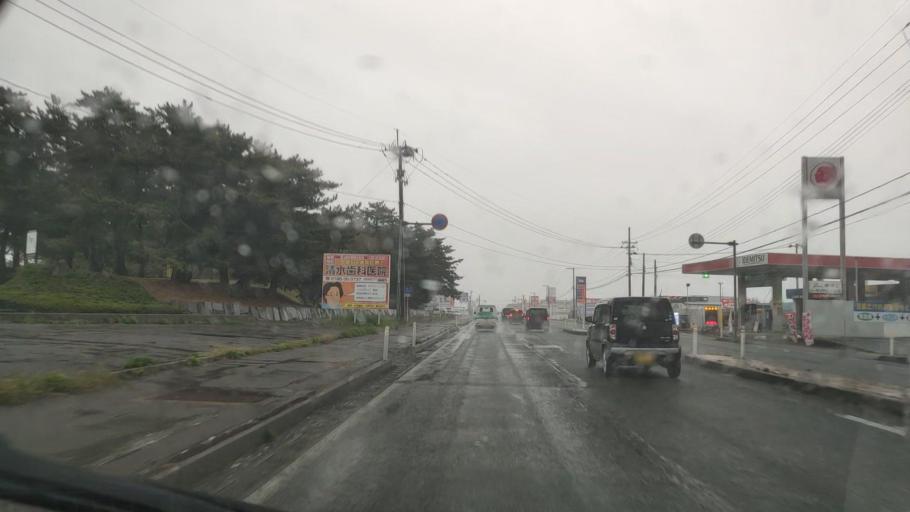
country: JP
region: Akita
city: Tenno
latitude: 39.9020
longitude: 139.9391
